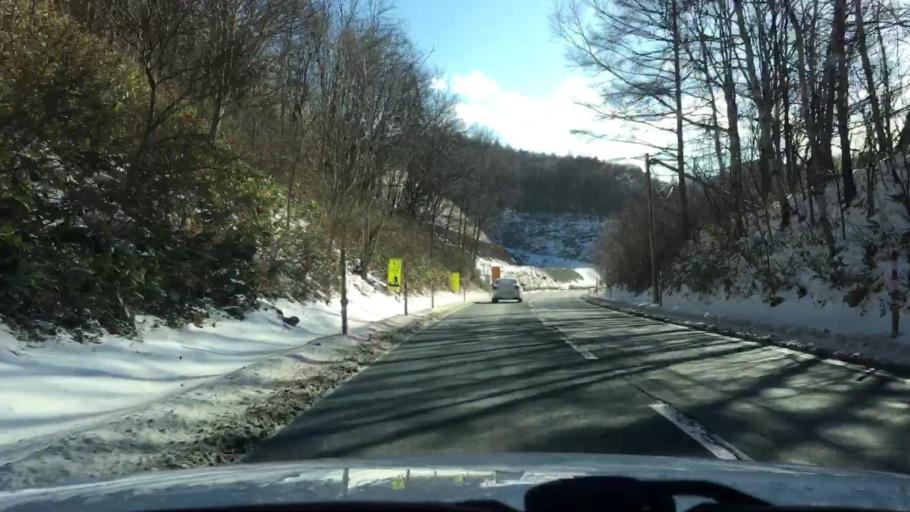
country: JP
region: Iwate
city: Morioka-shi
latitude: 39.6369
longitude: 141.4363
